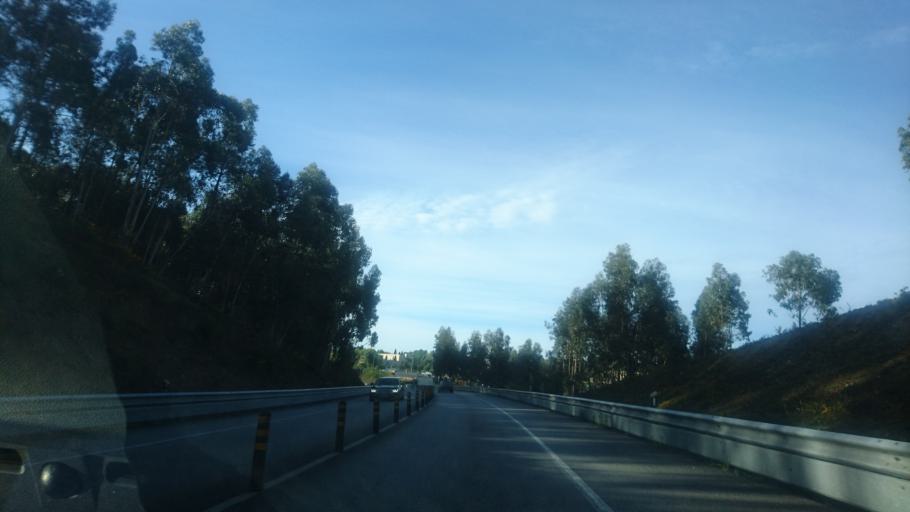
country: PT
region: Aveiro
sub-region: Santa Maria da Feira
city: Arrifana
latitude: 40.9212
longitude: -8.4903
